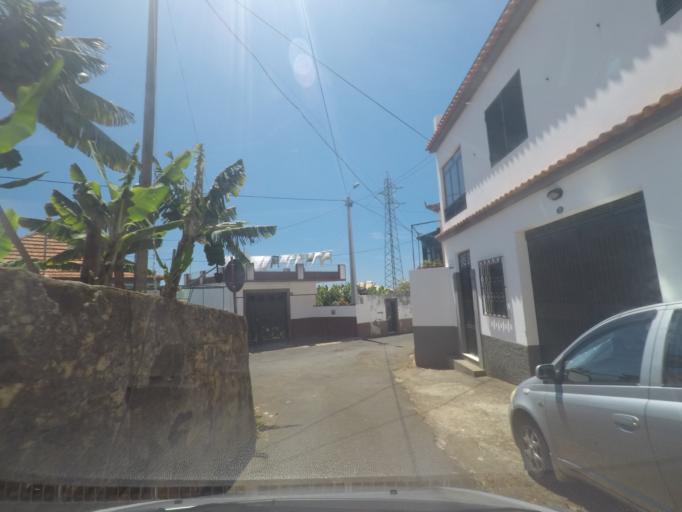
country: PT
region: Madeira
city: Camara de Lobos
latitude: 32.6546
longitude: -16.9688
